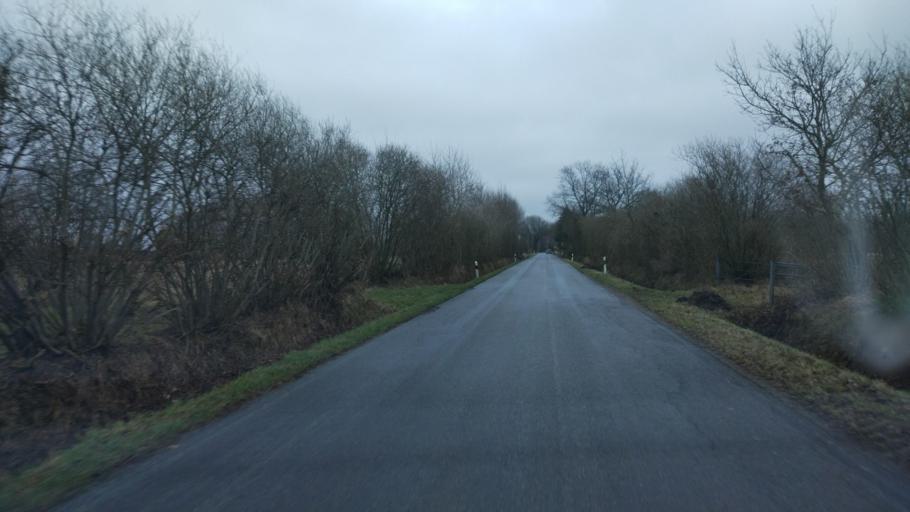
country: DE
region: Schleswig-Holstein
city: Ellingstedt
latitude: 54.4839
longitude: 9.4013
